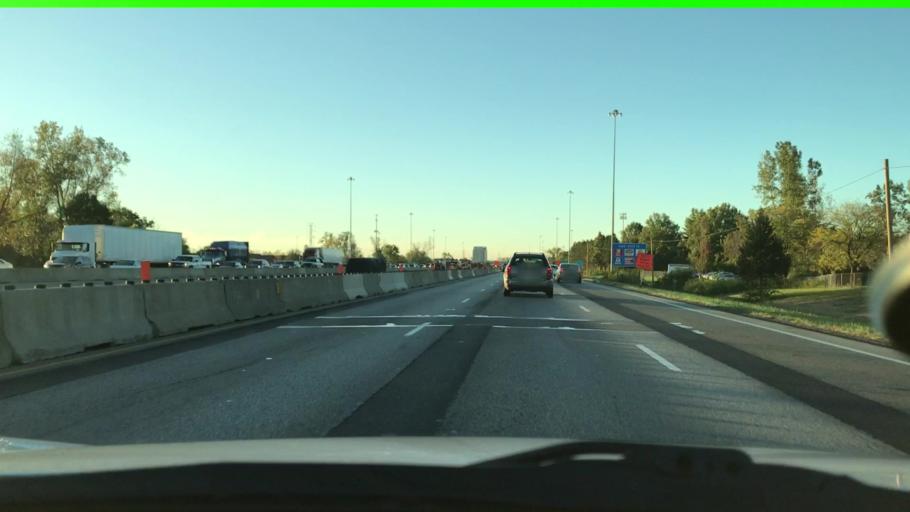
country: US
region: Ohio
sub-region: Franklin County
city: Hilliard
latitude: 40.0420
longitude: -83.1265
